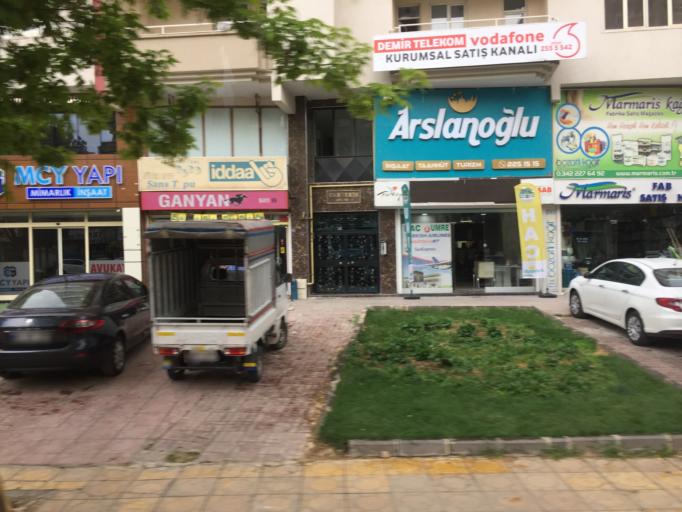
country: TR
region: Gaziantep
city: Gaziantep
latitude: 37.0719
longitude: 37.3721
